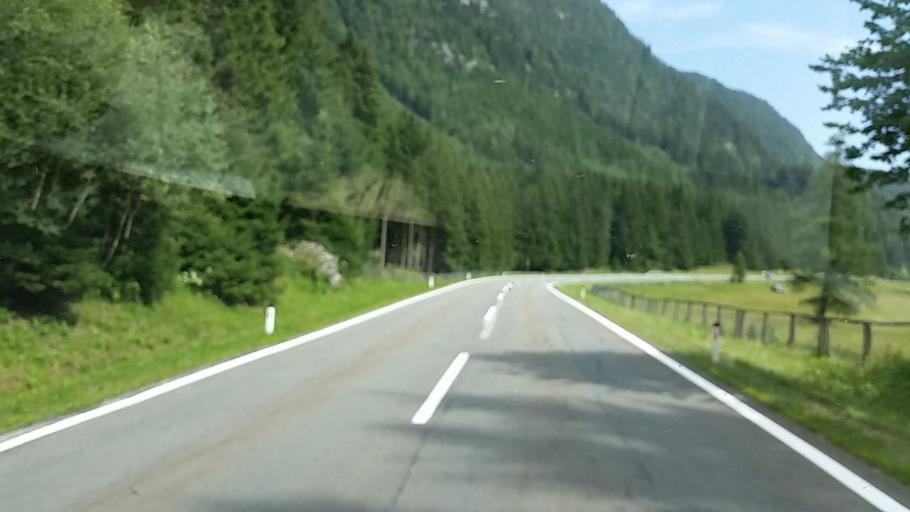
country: AT
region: Salzburg
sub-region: Politischer Bezirk Tamsweg
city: Mauterndorf
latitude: 47.1667
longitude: 13.6461
